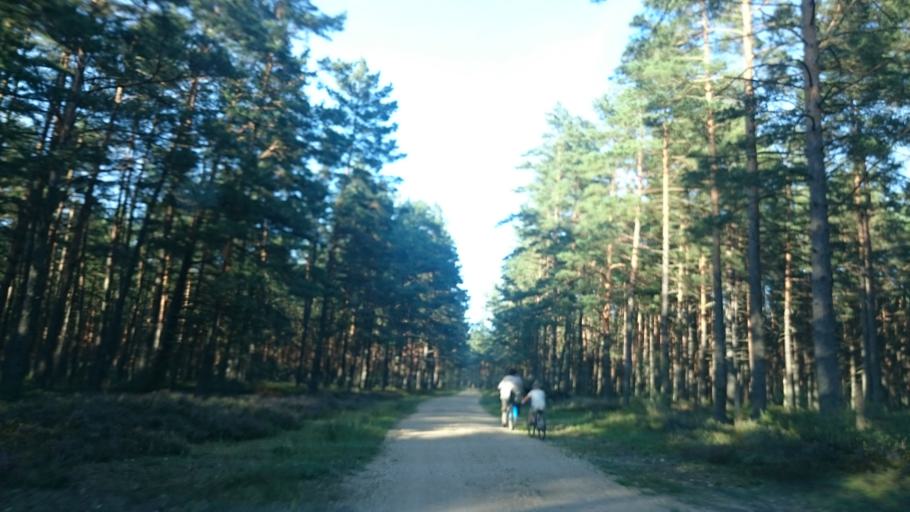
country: LV
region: Carnikava
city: Carnikava
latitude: 57.1085
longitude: 24.2374
